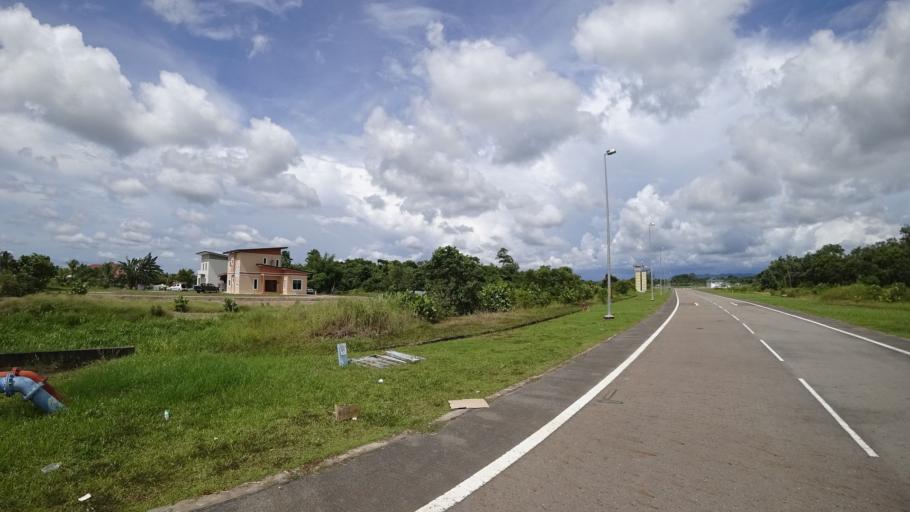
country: BN
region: Tutong
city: Tutong
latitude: 4.7496
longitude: 114.8182
